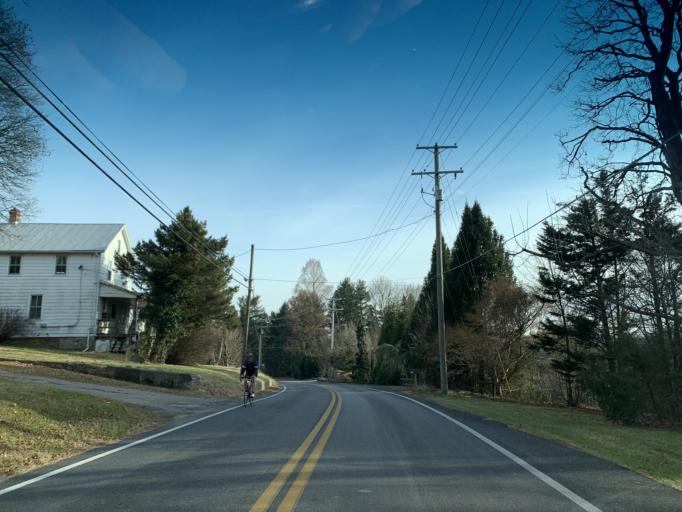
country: US
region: Maryland
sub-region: Carroll County
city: Hampstead
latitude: 39.6132
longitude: -76.8024
